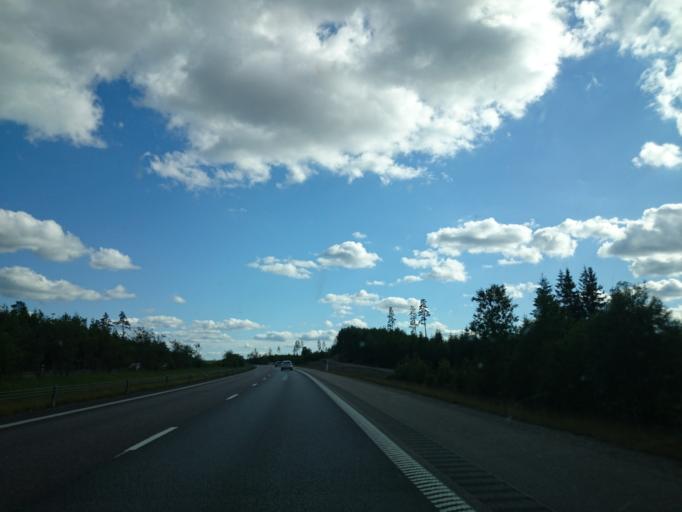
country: SE
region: Kronoberg
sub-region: Ljungby Kommun
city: Ljungby
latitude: 56.7421
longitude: 13.8546
